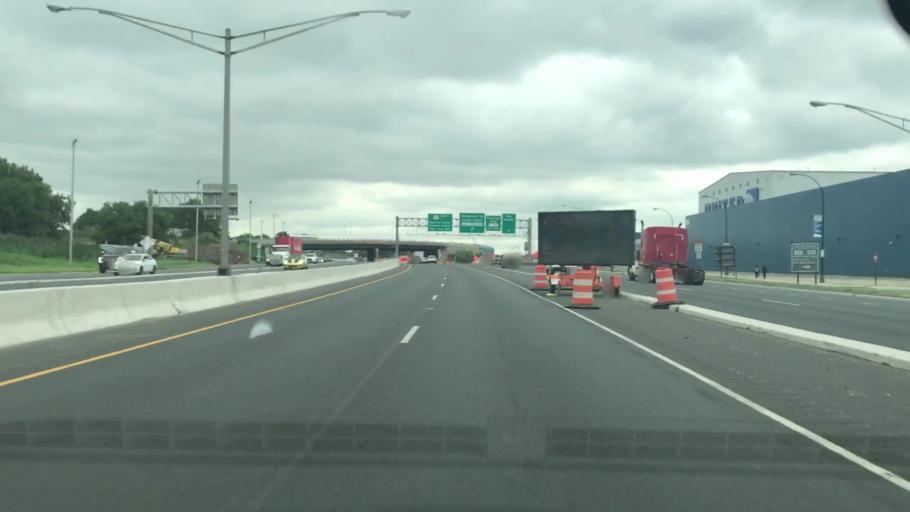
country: US
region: New Jersey
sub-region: Essex County
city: Newark
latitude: 40.7082
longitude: -74.1695
